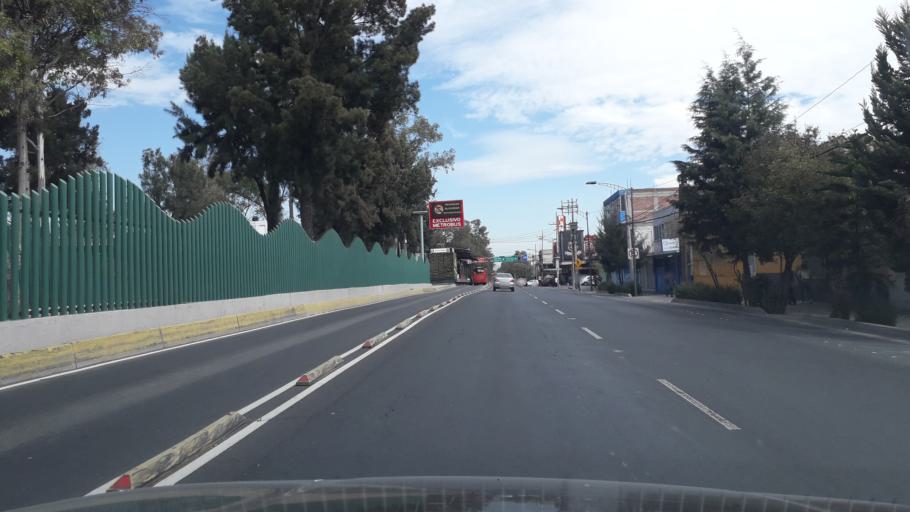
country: MX
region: Mexico City
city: Gustavo A. Madero
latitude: 19.4921
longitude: -99.0920
